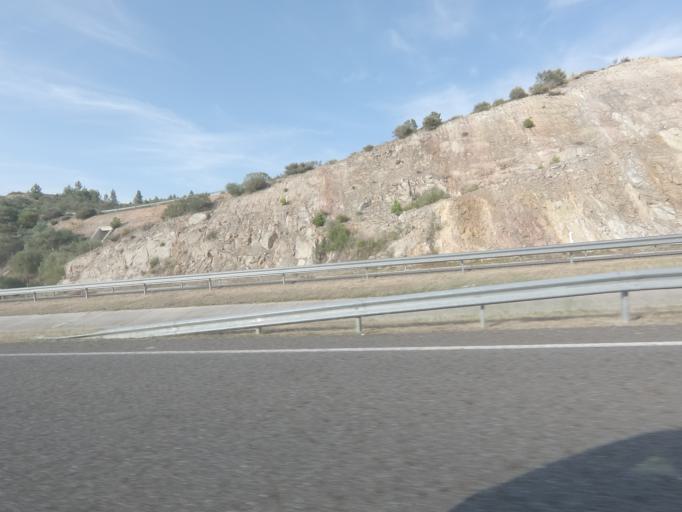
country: ES
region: Galicia
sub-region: Provincia de Ourense
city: Oimbra
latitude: 41.8573
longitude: -7.4242
